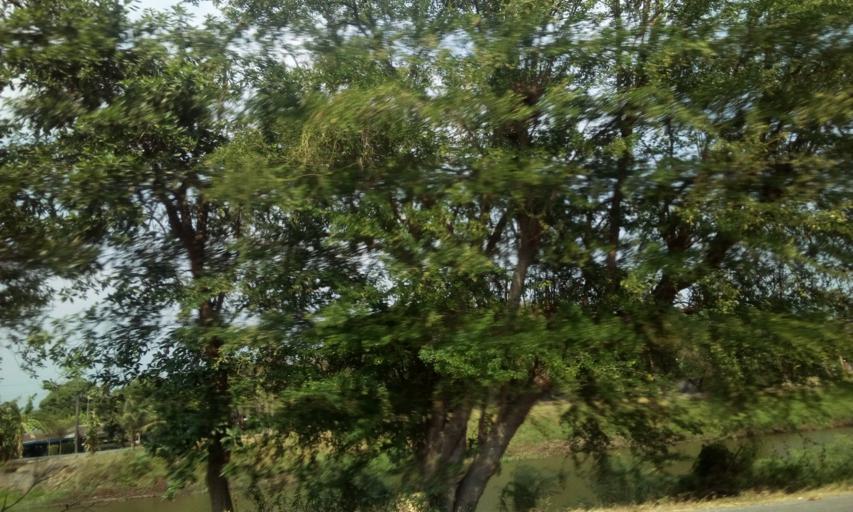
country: TH
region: Nakhon Nayok
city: Nakhon Nayok
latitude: 14.2093
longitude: 101.1807
